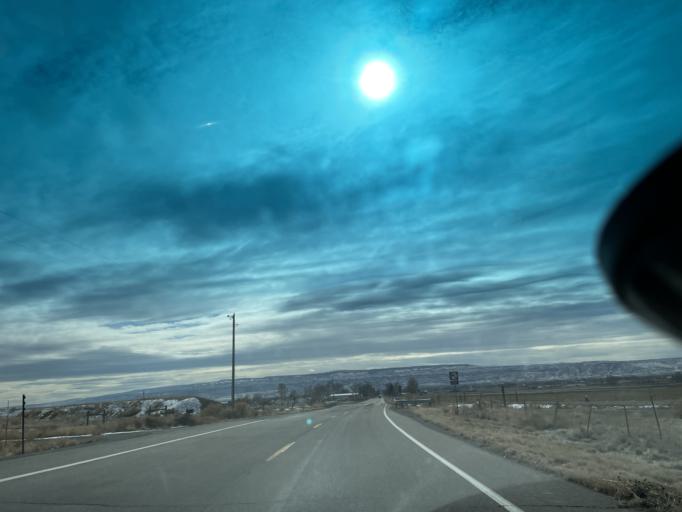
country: US
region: Colorado
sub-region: Mesa County
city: Loma
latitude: 39.2656
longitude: -108.8128
